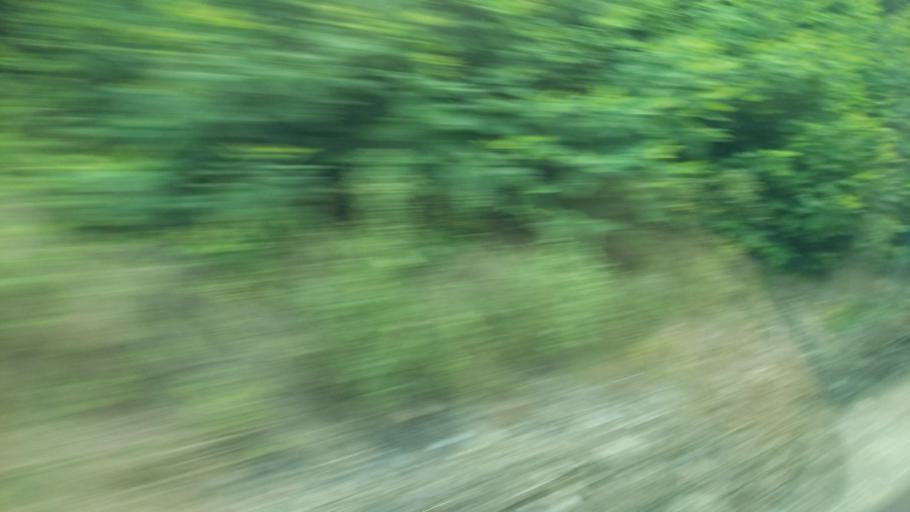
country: CZ
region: Central Bohemia
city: Cesky Brod
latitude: 50.0791
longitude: 14.8161
